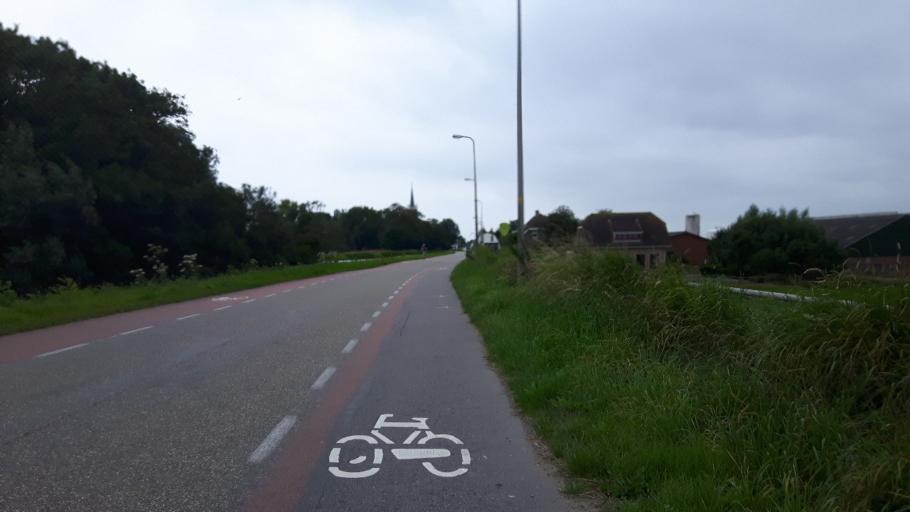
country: NL
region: South Holland
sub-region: Gemeente Kaag en Braassem
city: Leimuiden
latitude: 52.2140
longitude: 4.6699
